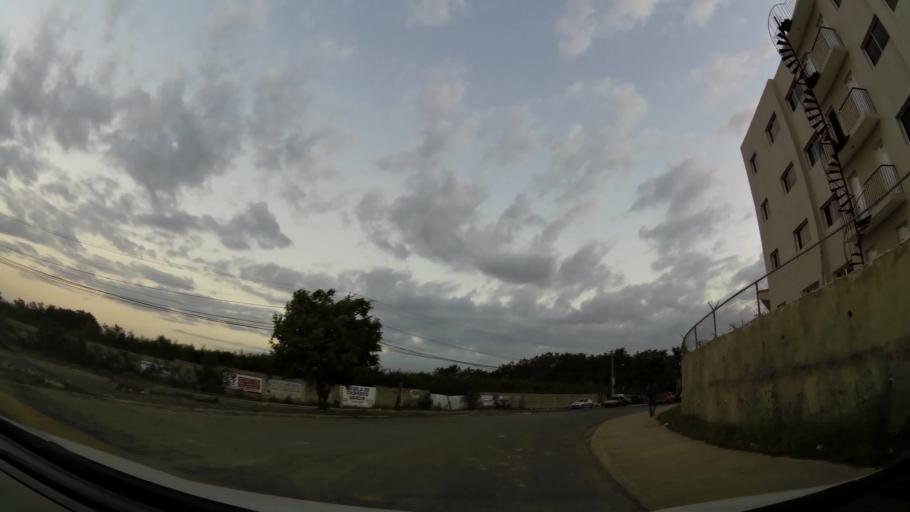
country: DO
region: Nacional
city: La Agustina
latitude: 18.5616
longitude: -69.9369
